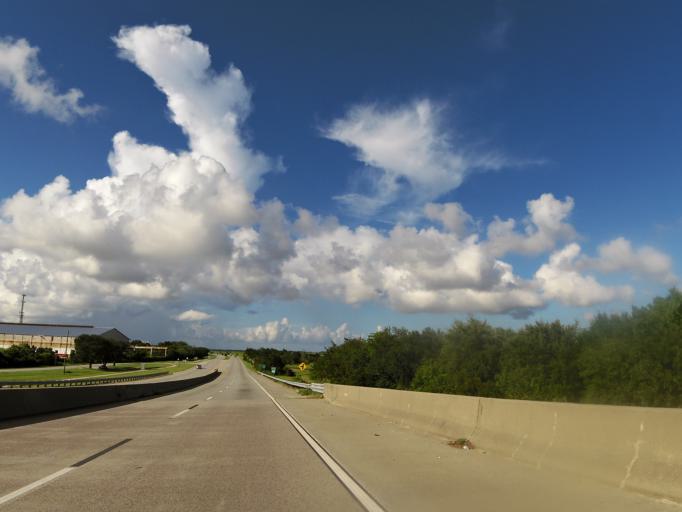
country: US
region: Georgia
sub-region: Glynn County
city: Brunswick
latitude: 31.1260
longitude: -81.4802
